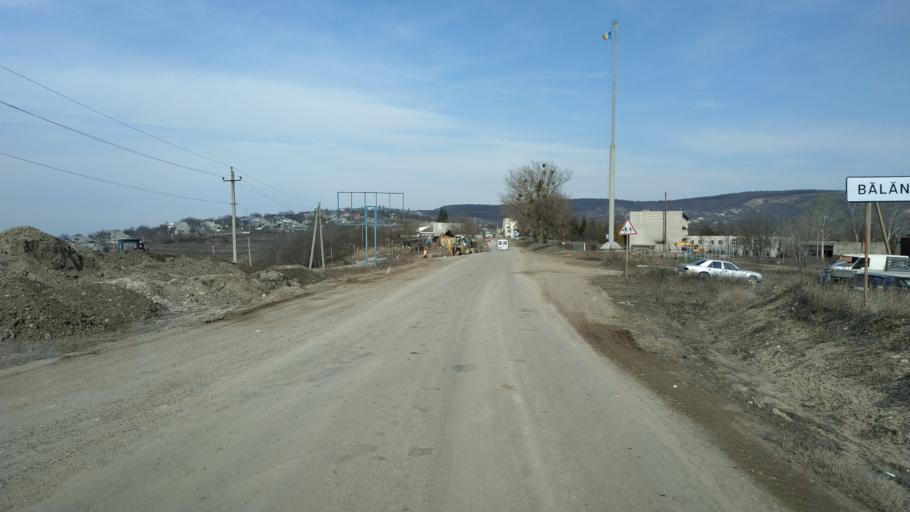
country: MD
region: Nisporeni
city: Nisporeni
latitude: 47.1923
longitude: 28.0666
